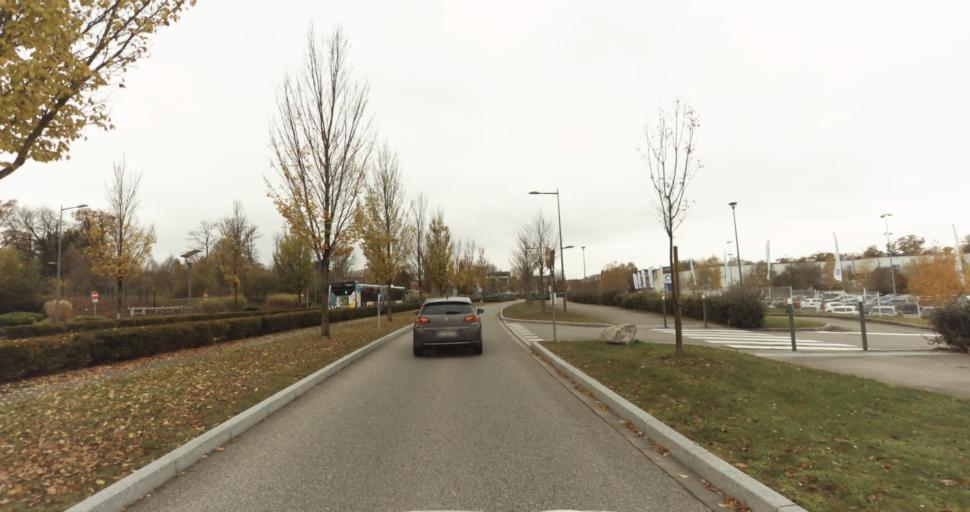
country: FR
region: Rhone-Alpes
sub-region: Departement de la Haute-Savoie
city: Seynod
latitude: 45.8785
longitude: 6.0950
